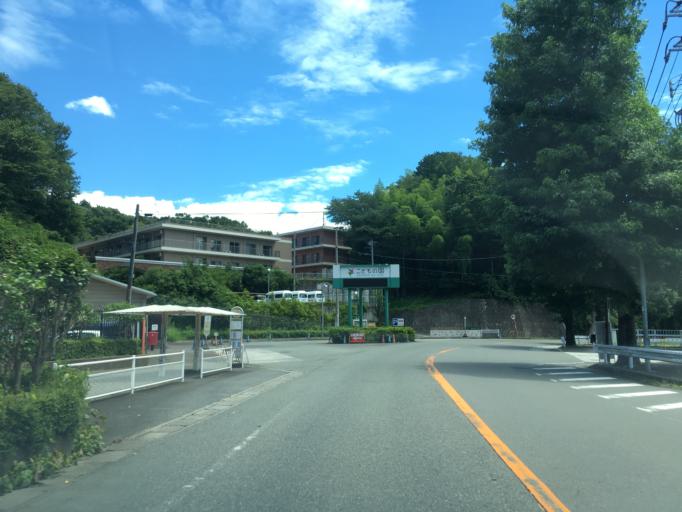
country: JP
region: Tokyo
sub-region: Machida-shi
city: Machida
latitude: 35.5596
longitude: 139.4870
